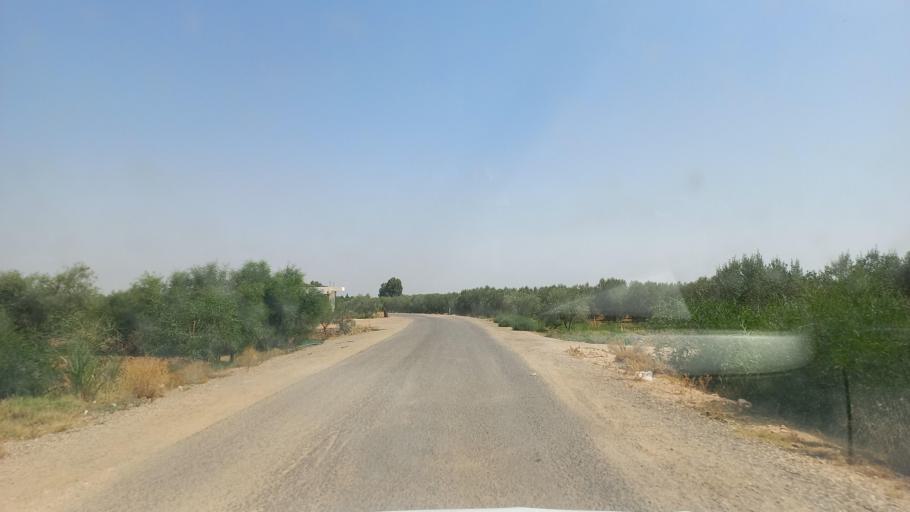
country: TN
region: Al Qasrayn
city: Kasserine
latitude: 35.2367
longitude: 9.0354
